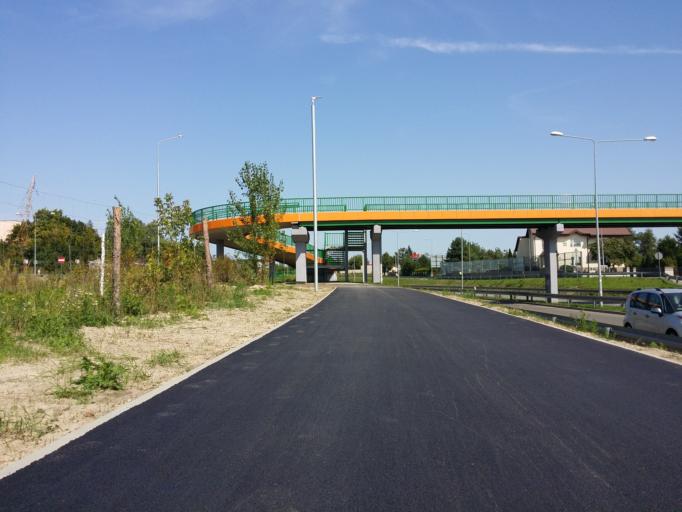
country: PL
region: Masovian Voivodeship
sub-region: Radom
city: Radom
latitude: 51.3718
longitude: 21.1621
